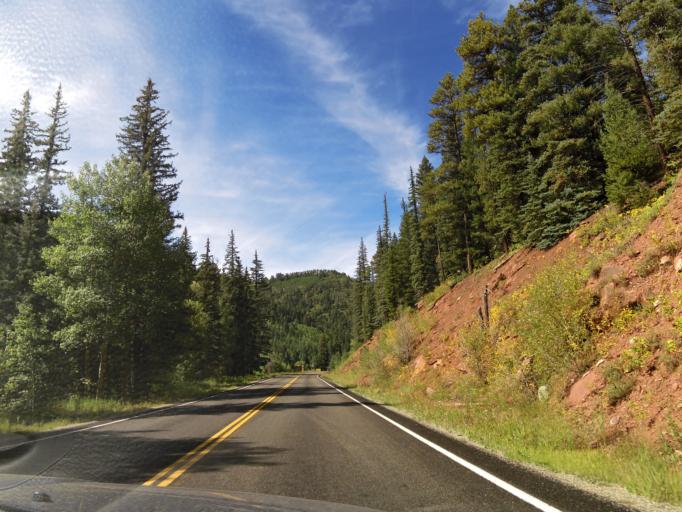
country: US
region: Colorado
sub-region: Montezuma County
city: Mancos
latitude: 37.5896
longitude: -108.1470
